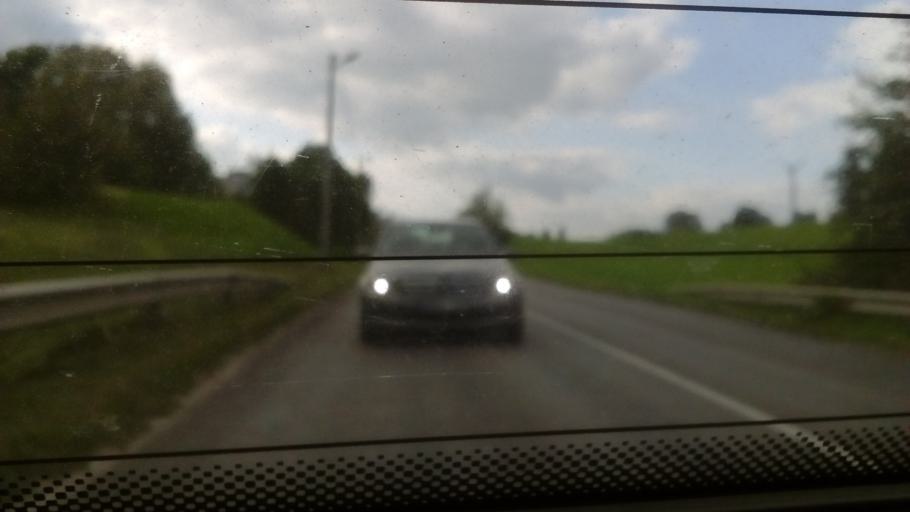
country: LT
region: Alytaus apskritis
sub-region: Alytus
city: Alytus
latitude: 54.4083
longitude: 24.0297
